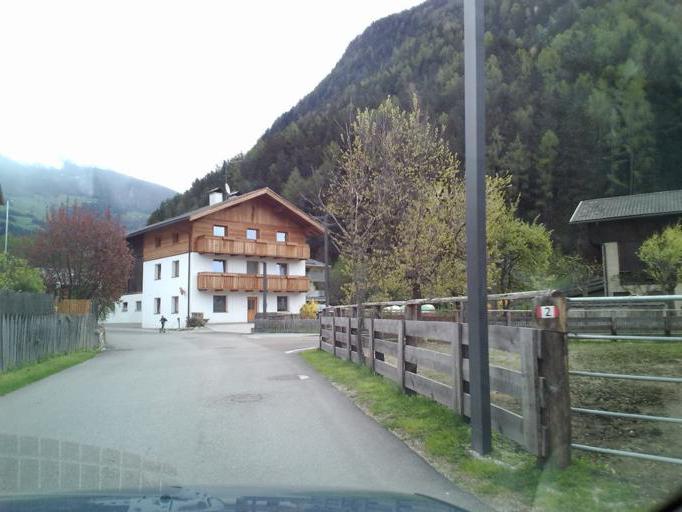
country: IT
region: Trentino-Alto Adige
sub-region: Bolzano
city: Campo Tures
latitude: 46.9029
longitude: 11.9570
